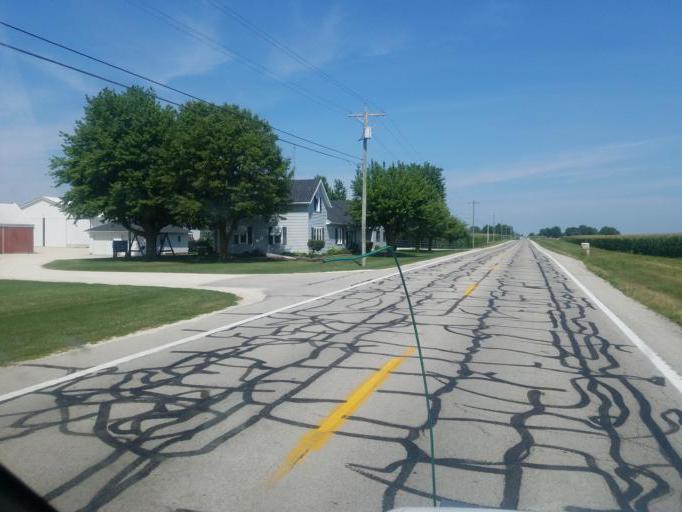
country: US
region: Ohio
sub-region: Auglaize County
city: Saint Marys
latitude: 40.4948
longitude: -84.4659
